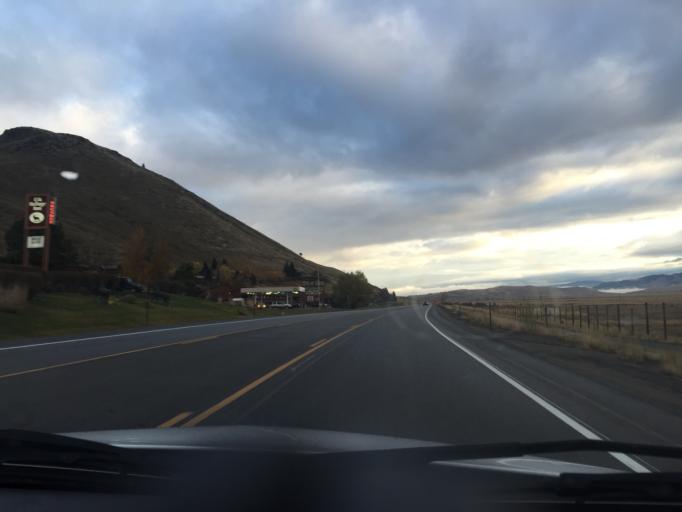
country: US
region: Wyoming
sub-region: Teton County
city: Jackson
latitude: 43.5048
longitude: -110.7579
